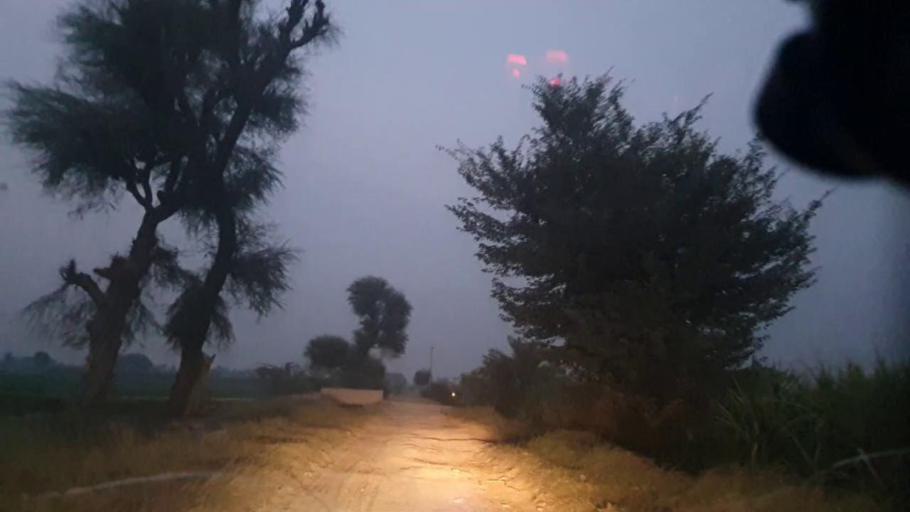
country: PK
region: Sindh
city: Hingorja
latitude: 27.2075
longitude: 68.3715
